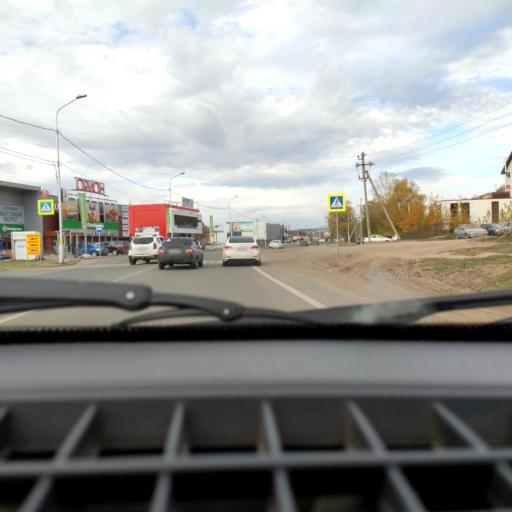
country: RU
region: Bashkortostan
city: Ufa
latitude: 54.6891
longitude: 55.9857
